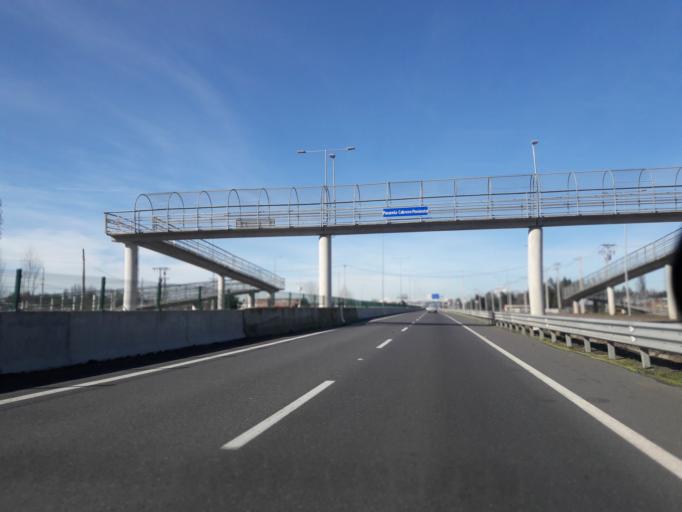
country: CL
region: Biobio
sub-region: Provincia de Biobio
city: Cabrero
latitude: -37.0340
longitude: -72.4174
